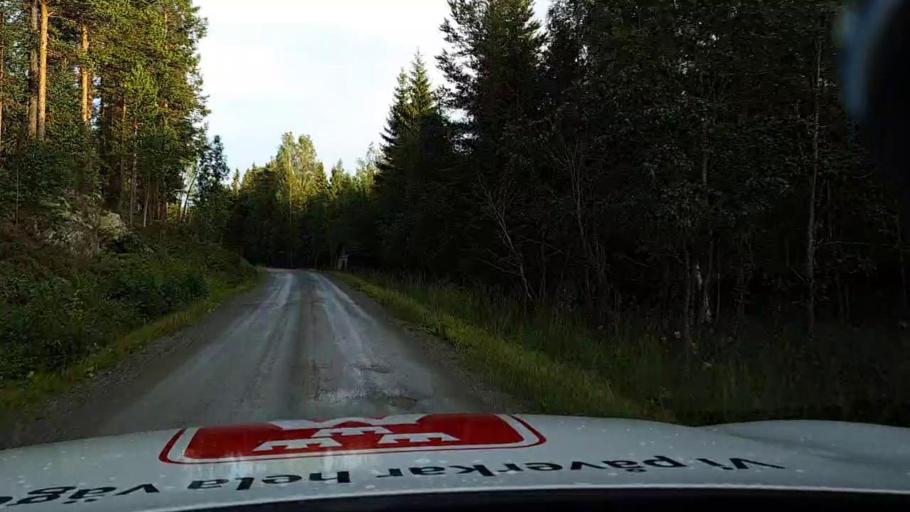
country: SE
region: Jaemtland
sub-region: Bergs Kommun
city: Hoverberg
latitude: 62.8627
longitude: 14.5303
